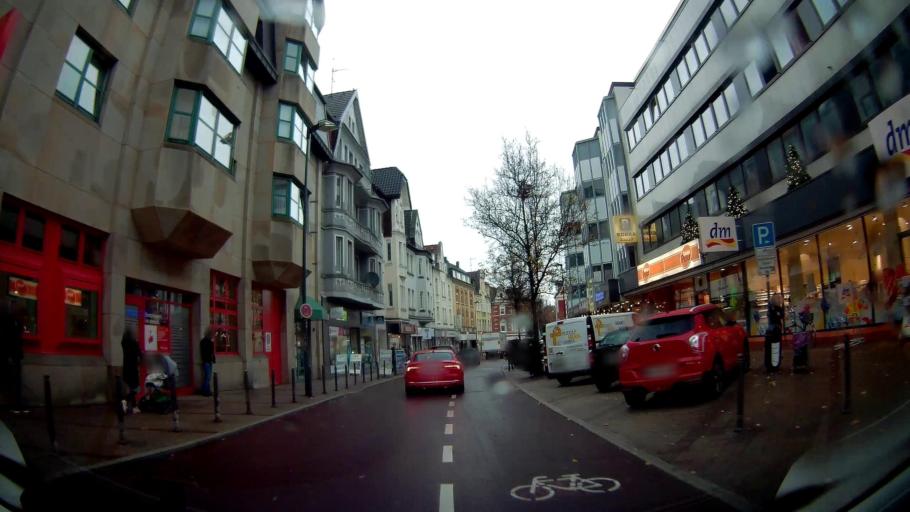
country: DE
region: North Rhine-Westphalia
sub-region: Regierungsbezirk Munster
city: Gelsenkirchen
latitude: 51.4668
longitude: 7.0806
